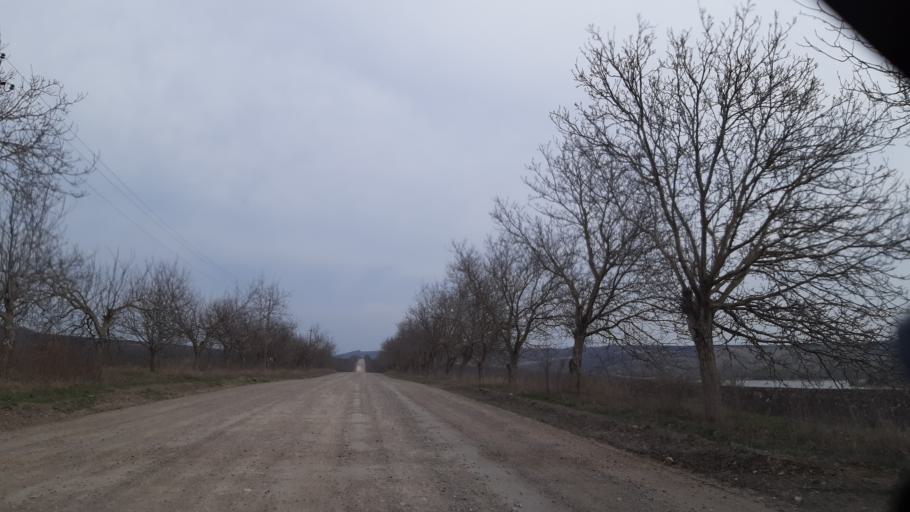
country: MD
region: Soldanesti
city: Soldanesti
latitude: 47.7003
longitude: 28.7233
